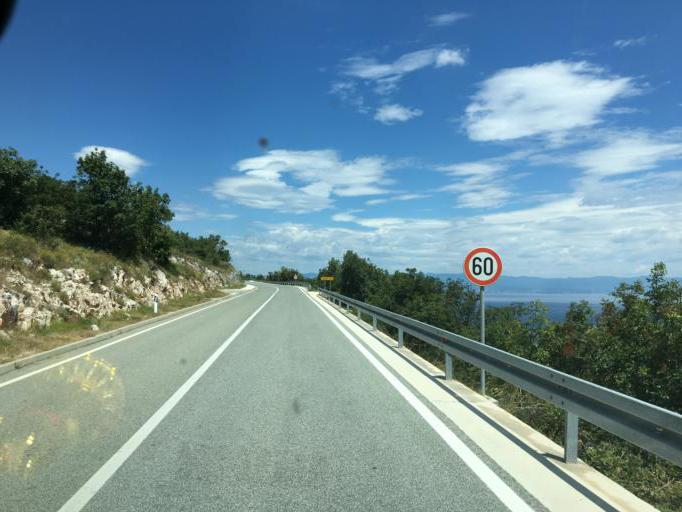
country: HR
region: Istarska
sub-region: Grad Labin
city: Rabac
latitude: 45.1392
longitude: 14.2114
